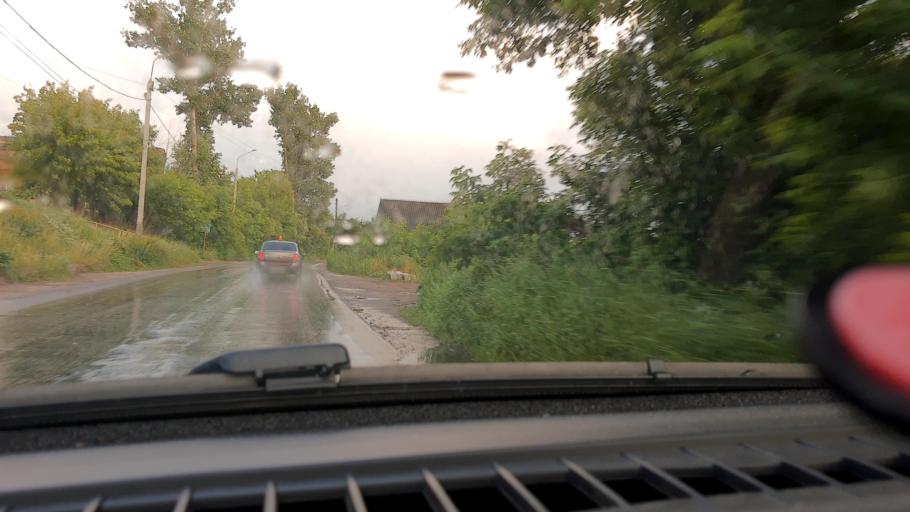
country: RU
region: Nizjnij Novgorod
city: Gorodets
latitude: 56.6618
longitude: 43.4599
